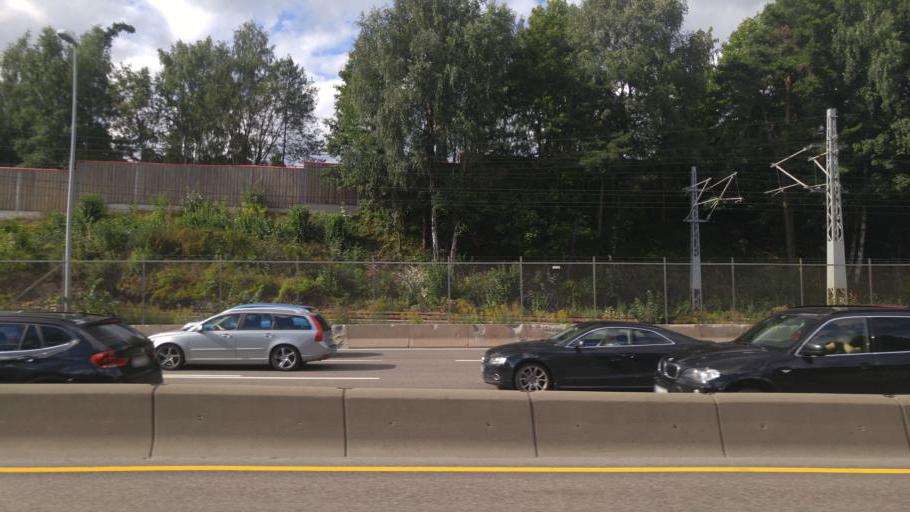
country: NO
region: Akershus
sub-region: Baerum
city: Lysaker
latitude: 59.9148
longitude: 10.6478
